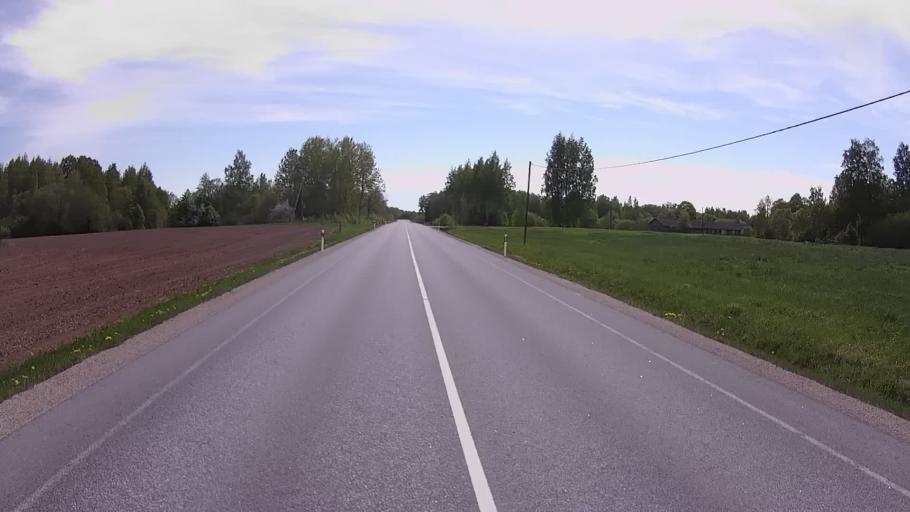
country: EE
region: Valgamaa
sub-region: Valga linn
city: Valga
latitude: 57.7438
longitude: 26.1422
